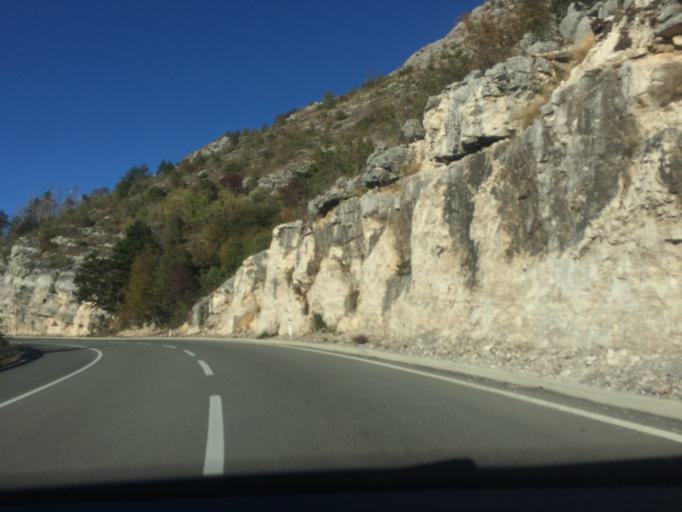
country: ME
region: Cetinje
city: Cetinje
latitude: 42.3839
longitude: 18.9634
